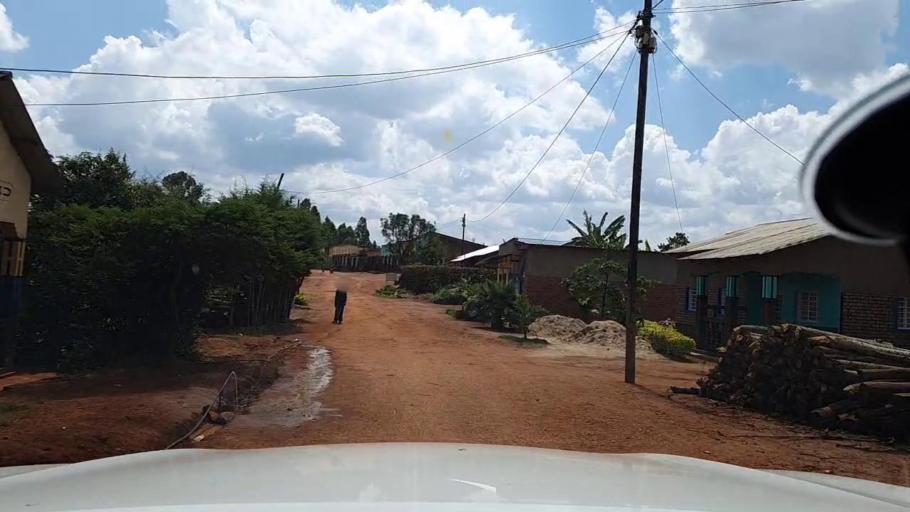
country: RW
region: Southern Province
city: Gitarama
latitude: -1.8349
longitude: 29.8344
